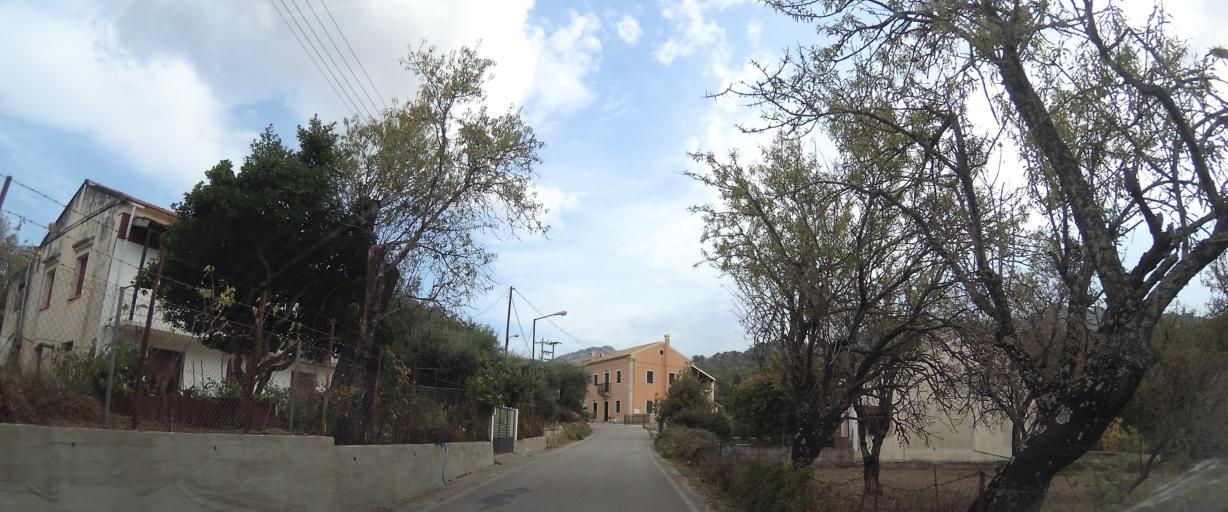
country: GR
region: Ionian Islands
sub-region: Nomos Kerkyras
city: Acharavi
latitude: 39.7863
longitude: 19.8783
